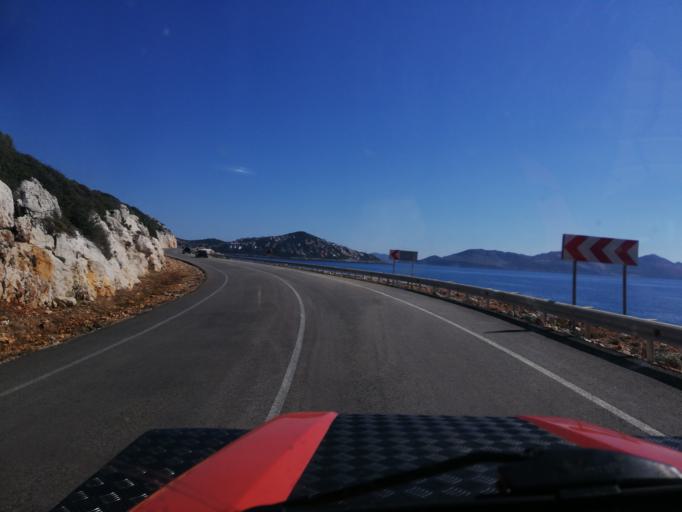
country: GR
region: South Aegean
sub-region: Nomos Dodekanisou
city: Megisti
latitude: 36.2045
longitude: 29.5713
